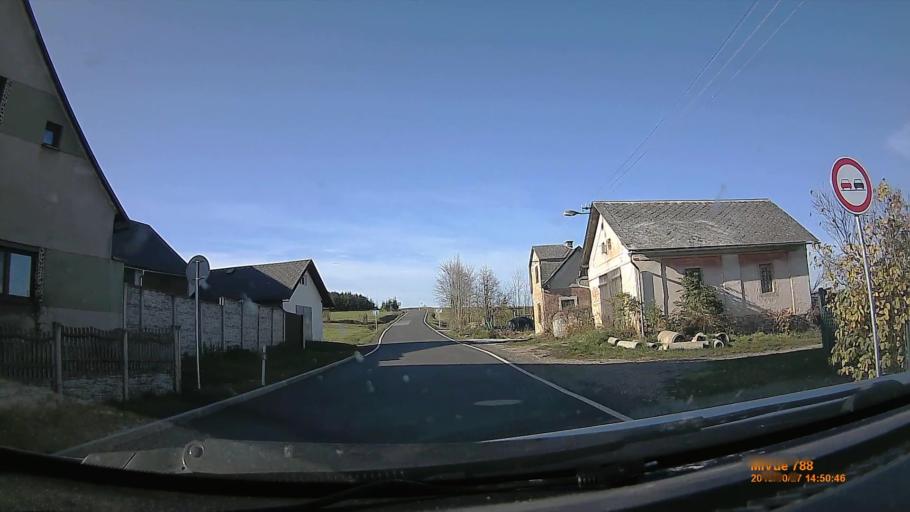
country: CZ
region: Pardubicky
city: Cervena Voda
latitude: 50.0495
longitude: 16.7267
